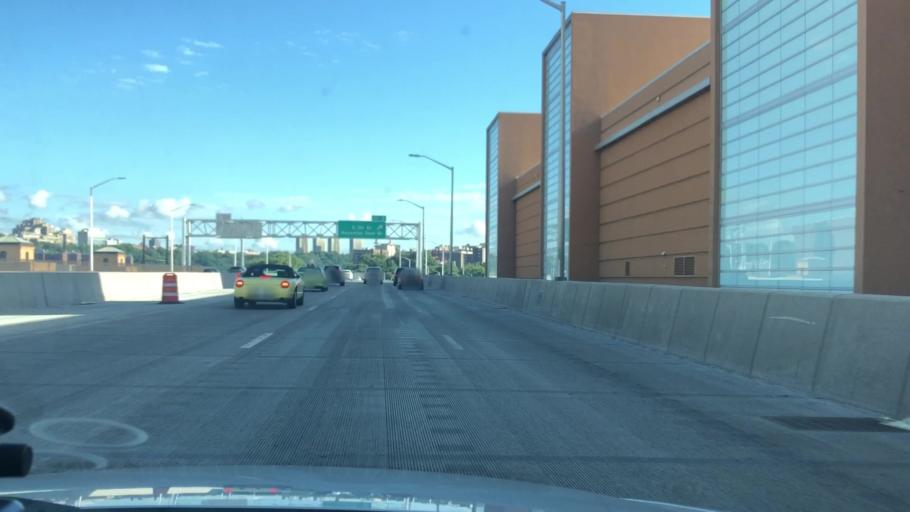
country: US
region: New York
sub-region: New York County
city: Inwood
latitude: 40.8233
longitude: -73.9309
